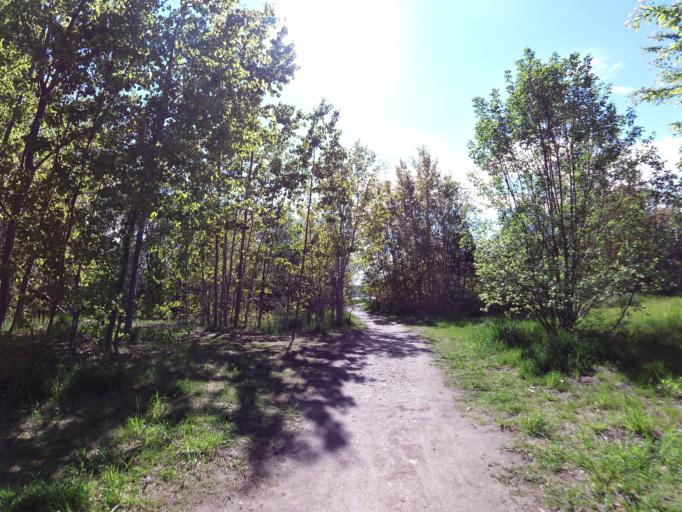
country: LT
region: Vilnius County
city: Seskine
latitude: 54.7210
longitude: 25.2573
